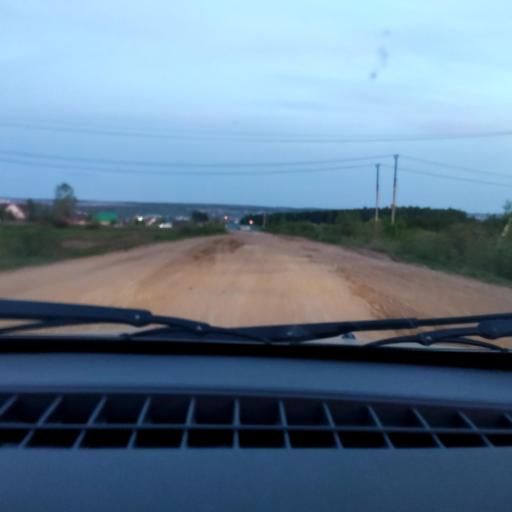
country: RU
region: Bashkortostan
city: Iglino
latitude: 54.8460
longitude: 56.4021
